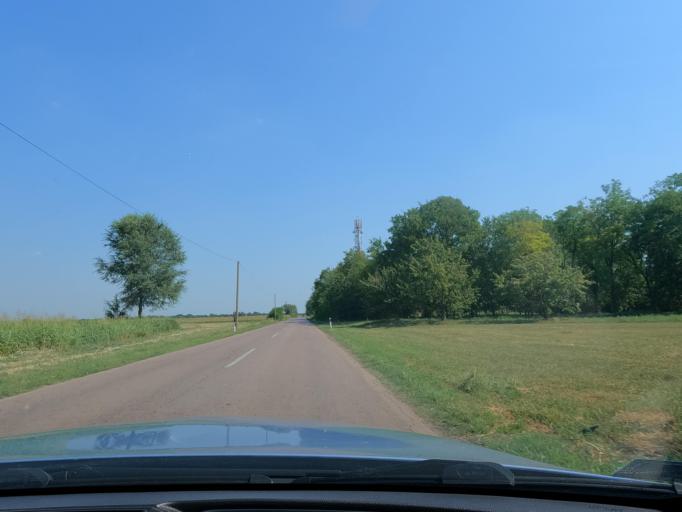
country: RS
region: Autonomna Pokrajina Vojvodina
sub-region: Severnobacki Okrug
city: Mali Igos
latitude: 45.7700
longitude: 19.7356
